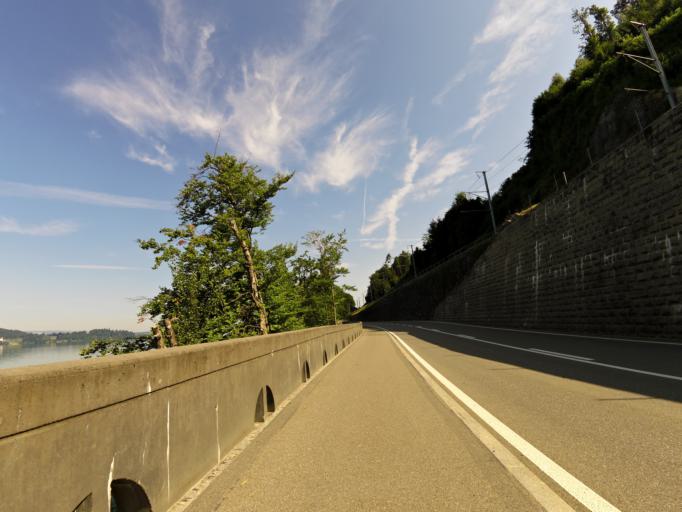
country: CH
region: Zug
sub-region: Zug
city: Walchwil
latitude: 47.1190
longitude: 8.4968
